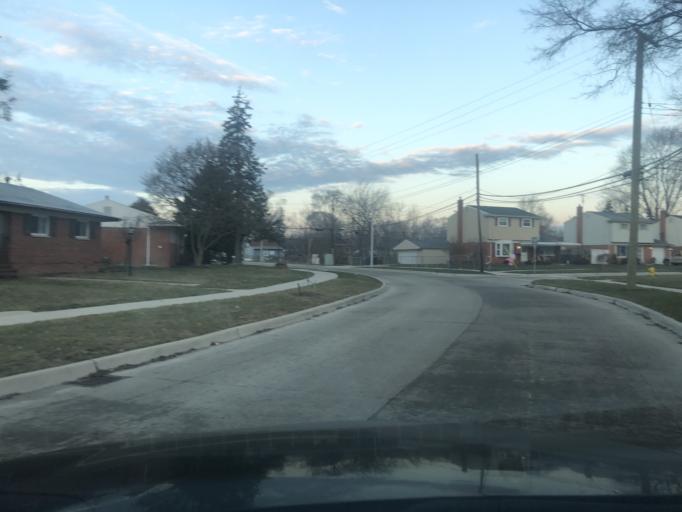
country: US
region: Michigan
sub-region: Wayne County
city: Garden City
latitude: 42.2998
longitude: -83.3472
